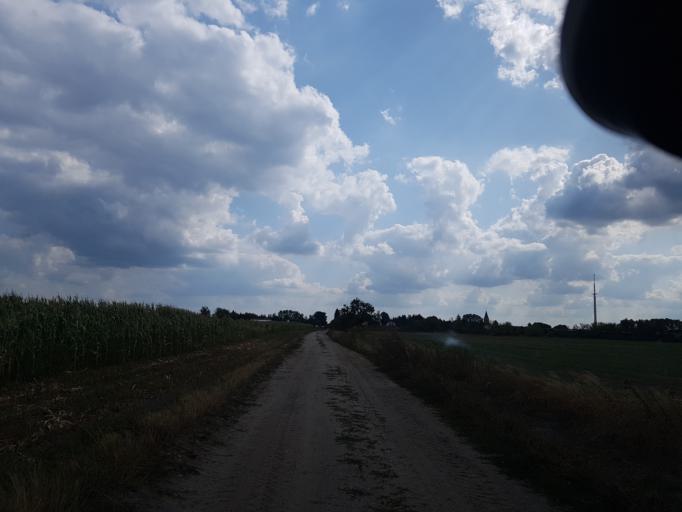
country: DE
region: Brandenburg
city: Calau
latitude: 51.7562
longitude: 13.9515
